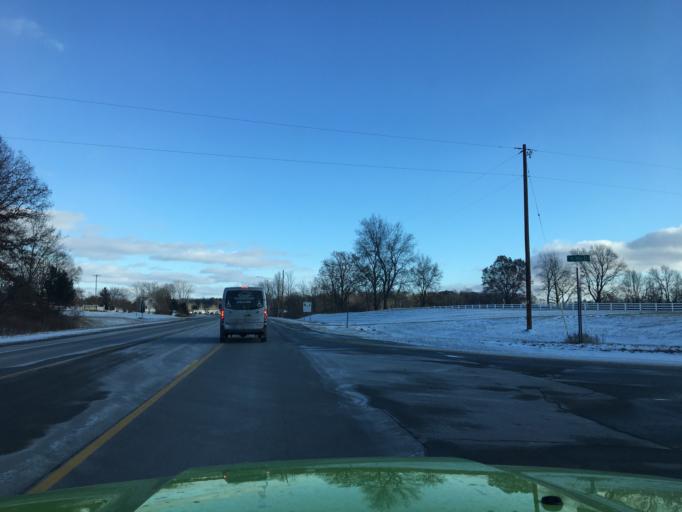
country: US
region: Michigan
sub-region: Kent County
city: Cedar Springs
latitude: 43.1761
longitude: -85.5322
